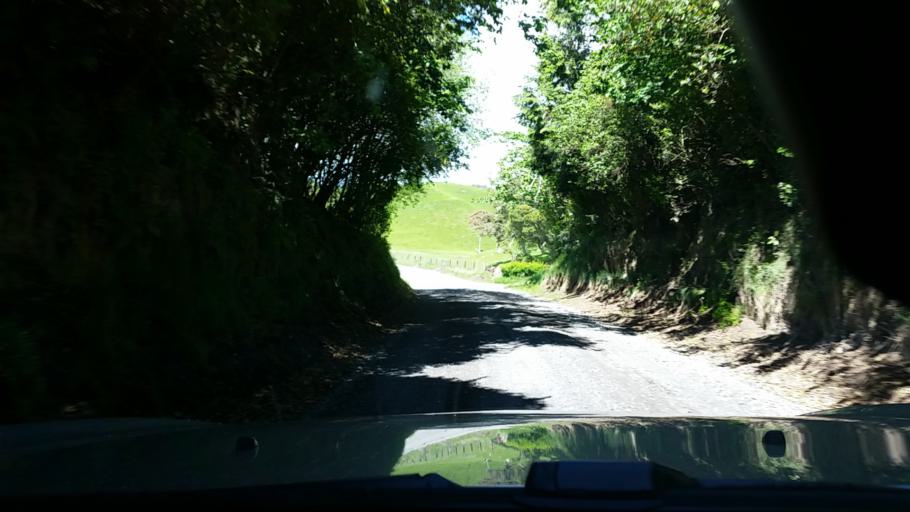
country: NZ
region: Bay of Plenty
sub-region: Rotorua District
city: Rotorua
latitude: -38.3592
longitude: 176.1229
